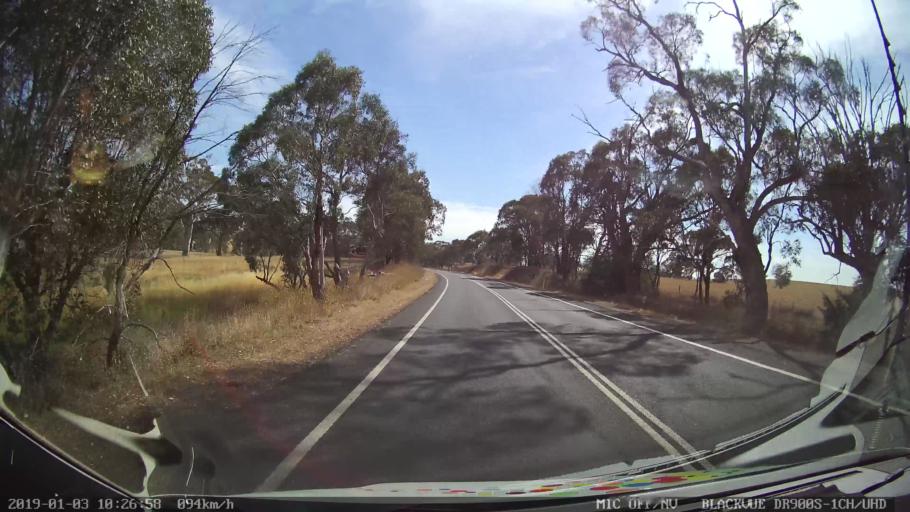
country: AU
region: New South Wales
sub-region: Young
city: Young
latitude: -34.4078
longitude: 148.2553
